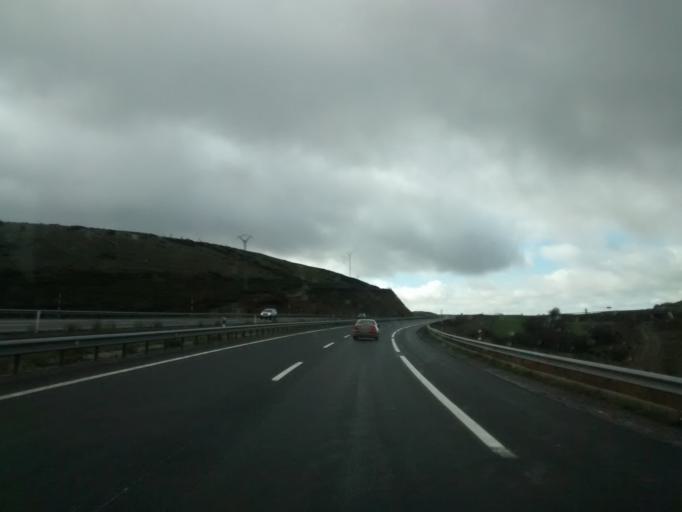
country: ES
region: Cantabria
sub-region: Provincia de Cantabria
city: Mataporquera
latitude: 42.9009
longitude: -4.1207
